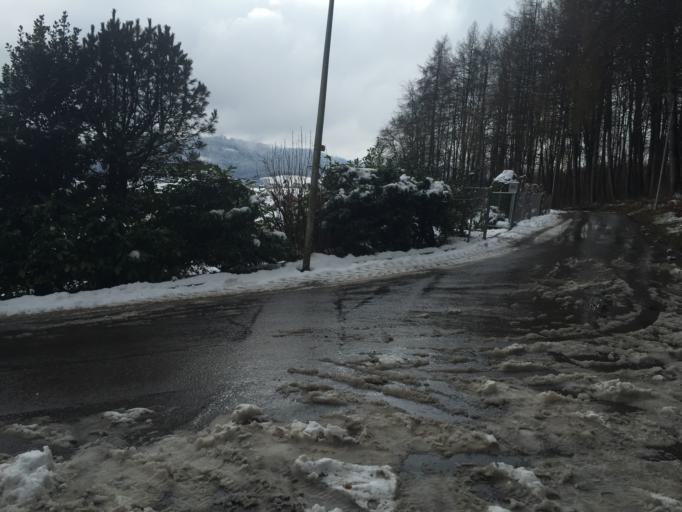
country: CH
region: Bern
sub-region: Bern-Mittelland District
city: Koniz
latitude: 46.9288
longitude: 7.4070
